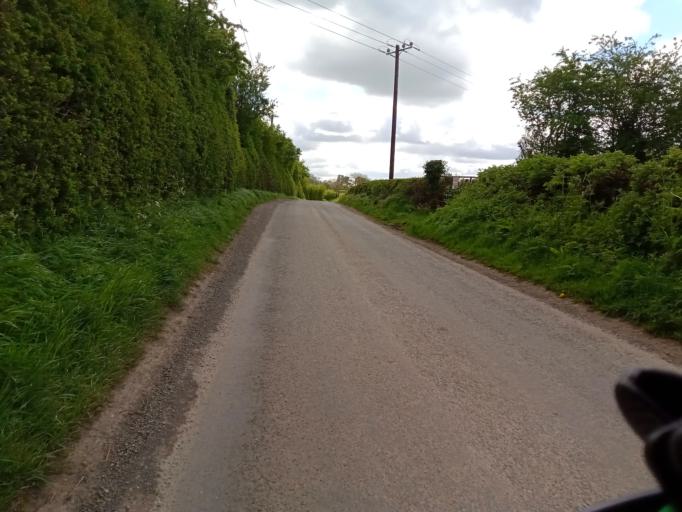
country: IE
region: Leinster
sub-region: Kilkenny
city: Thomastown
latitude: 52.5956
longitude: -7.1519
